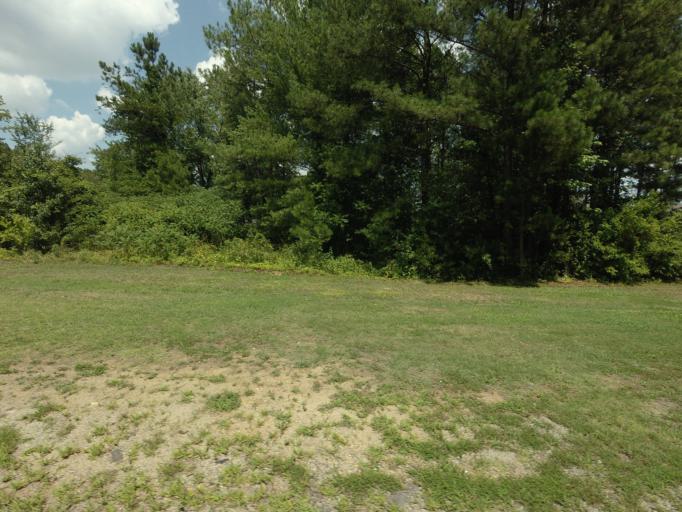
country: US
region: Georgia
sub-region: Fulton County
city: Johns Creek
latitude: 34.0590
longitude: -84.2063
